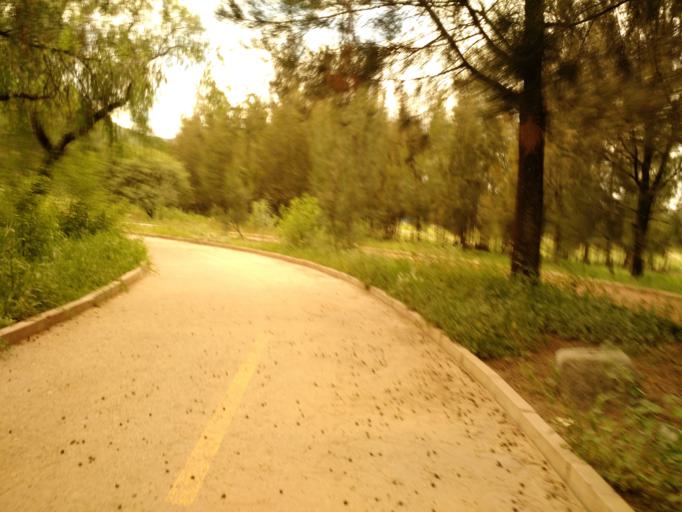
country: BO
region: Cochabamba
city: Cochabamba
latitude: -17.4024
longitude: -66.1330
